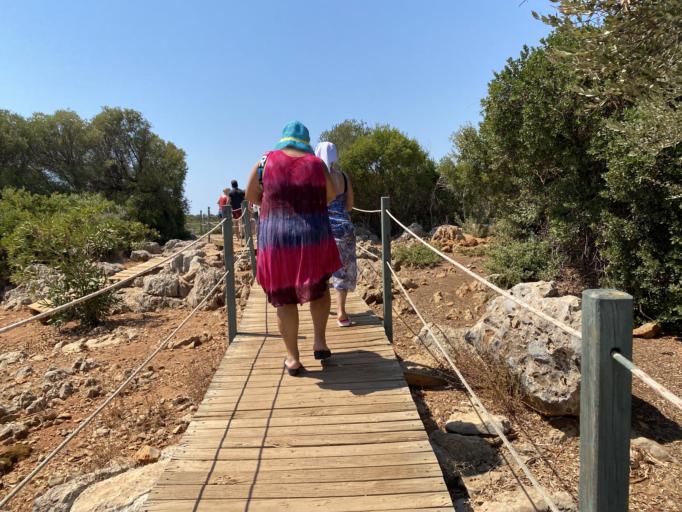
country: TR
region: Mugla
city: Yerkesik
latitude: 36.9936
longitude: 28.2045
